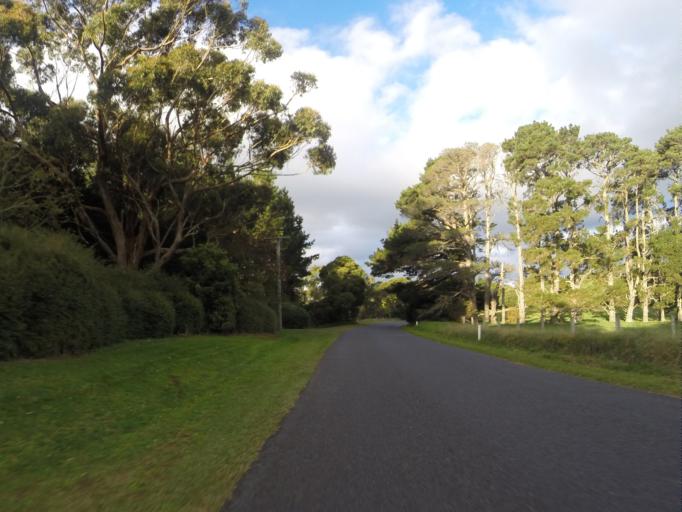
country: AU
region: New South Wales
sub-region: Shoalhaven Shire
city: Kangaroo Valley
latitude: -34.6004
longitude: 150.5557
